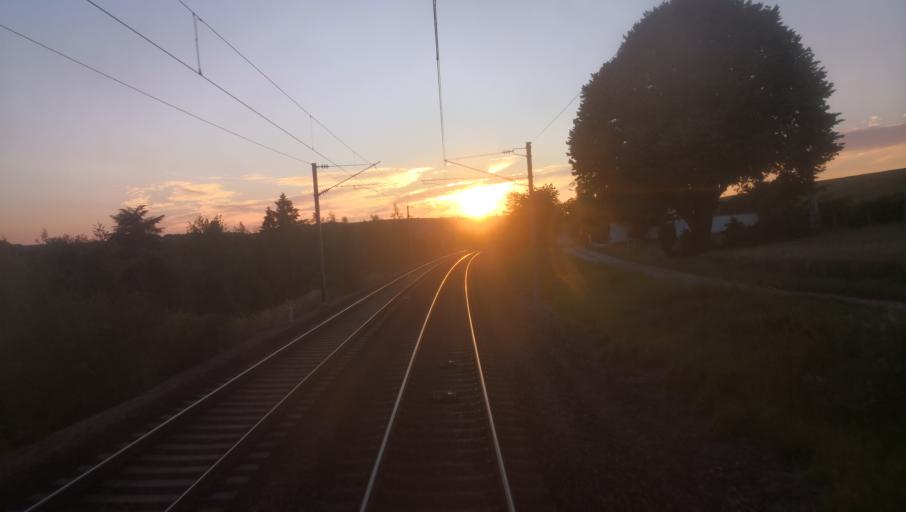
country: FR
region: Haute-Normandie
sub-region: Departement de l'Eure
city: Bueil
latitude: 48.9219
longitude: 1.4493
